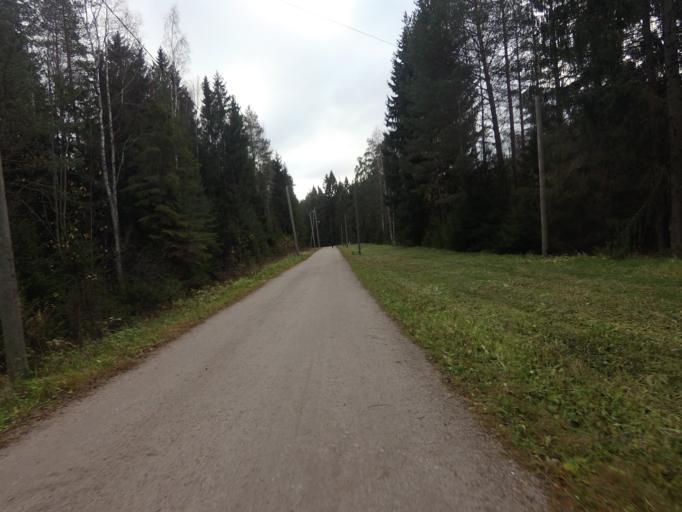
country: FI
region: Uusimaa
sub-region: Helsinki
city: Kauniainen
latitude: 60.1862
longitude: 24.6940
